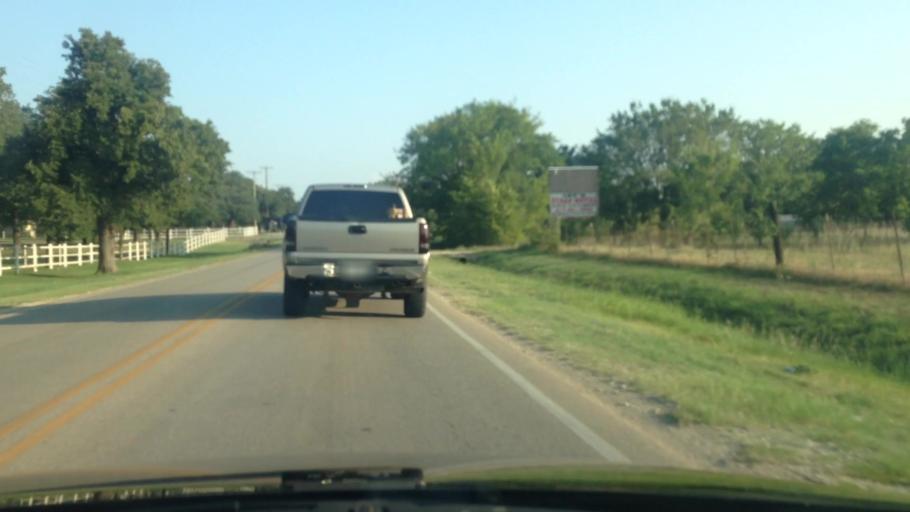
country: US
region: Texas
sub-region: Tarrant County
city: Everman
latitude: 32.6125
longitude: -97.2687
